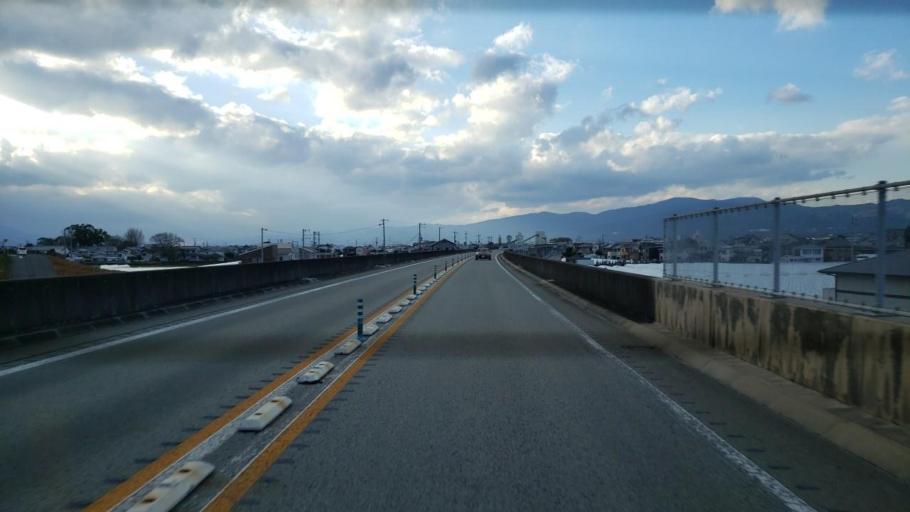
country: JP
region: Tokushima
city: Ishii
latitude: 34.1128
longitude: 134.4996
